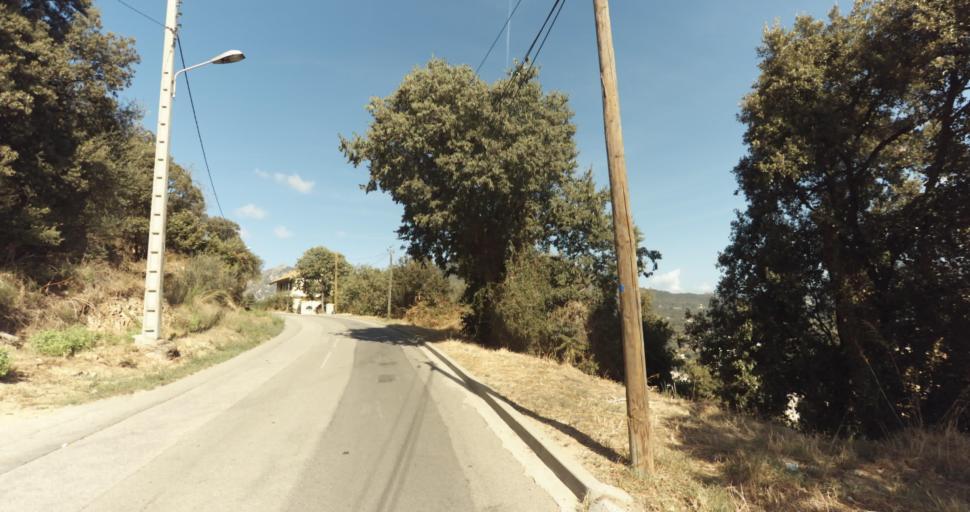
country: FR
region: Corsica
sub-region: Departement de la Corse-du-Sud
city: Ajaccio
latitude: 41.9247
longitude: 8.7288
